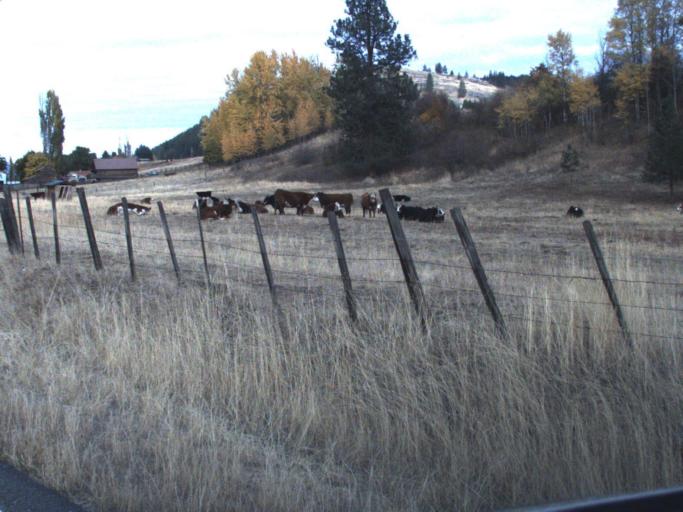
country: US
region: Washington
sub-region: Stevens County
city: Kettle Falls
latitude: 48.7457
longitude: -118.0483
